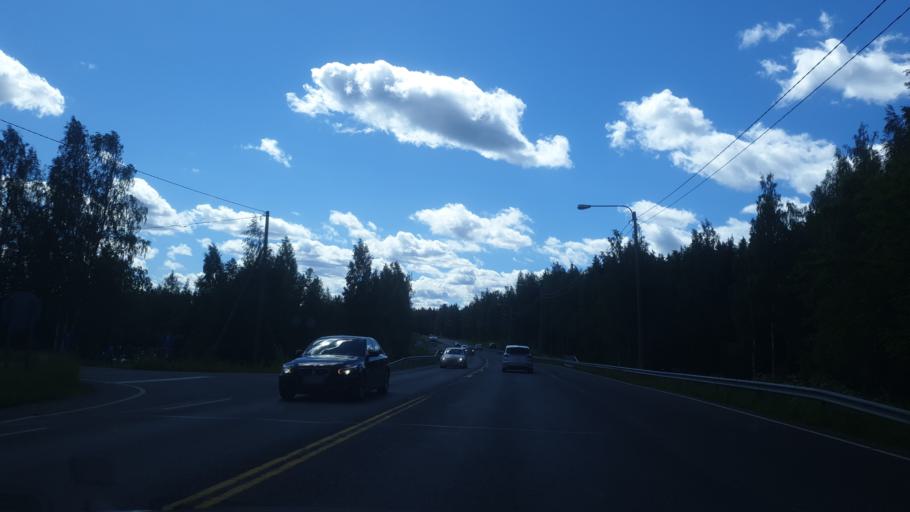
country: FI
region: Northern Savo
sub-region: Varkaus
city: Leppaevirta
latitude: 62.5946
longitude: 27.6060
